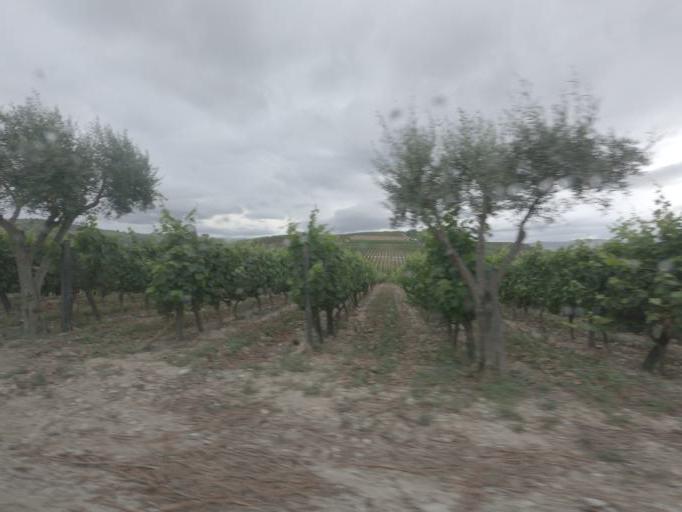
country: PT
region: Vila Real
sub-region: Sabrosa
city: Sabrosa
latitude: 41.2433
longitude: -7.4980
